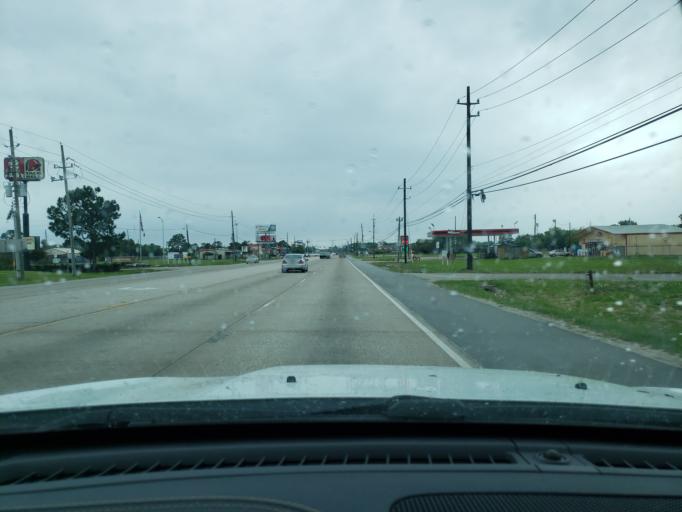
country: US
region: Texas
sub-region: Chambers County
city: Mont Belvieu
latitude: 29.8133
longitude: -94.9015
